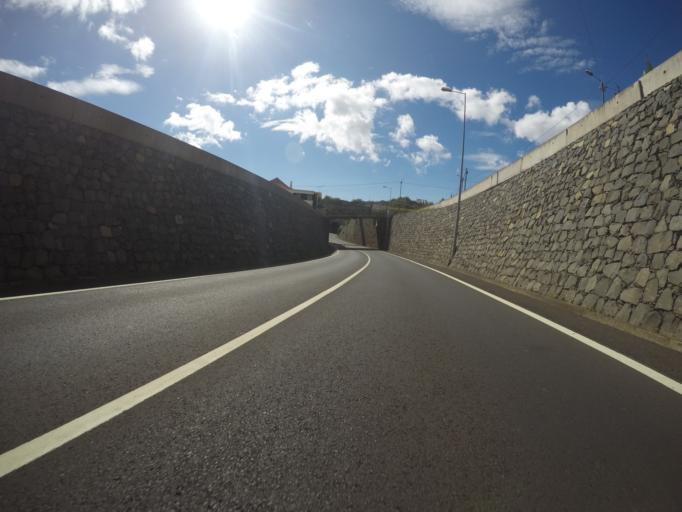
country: PT
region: Madeira
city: Canico
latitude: 32.6504
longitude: -16.8531
